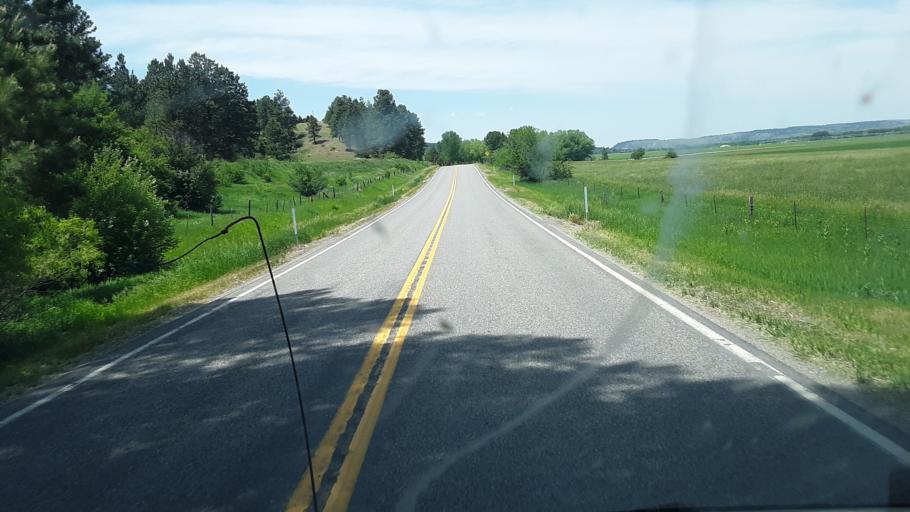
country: US
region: Montana
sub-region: Stillwater County
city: Columbus
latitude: 45.6037
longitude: -109.2016
